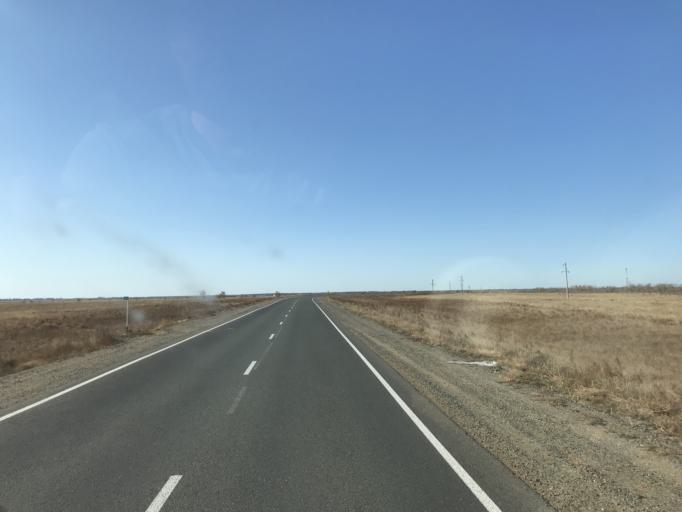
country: KZ
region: Pavlodar
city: Kurchatov
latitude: 51.0258
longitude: 79.1516
